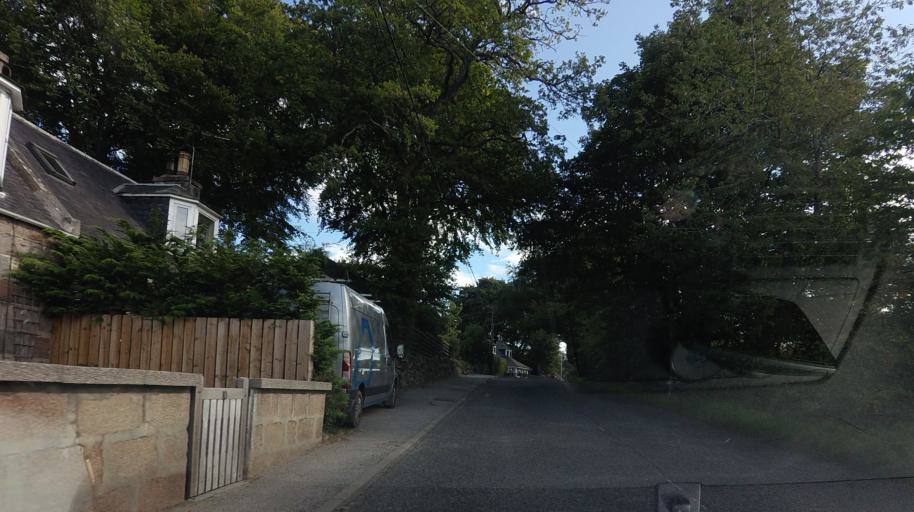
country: GB
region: Scotland
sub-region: Aberdeenshire
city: Torphins
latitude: 57.1279
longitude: -2.6820
